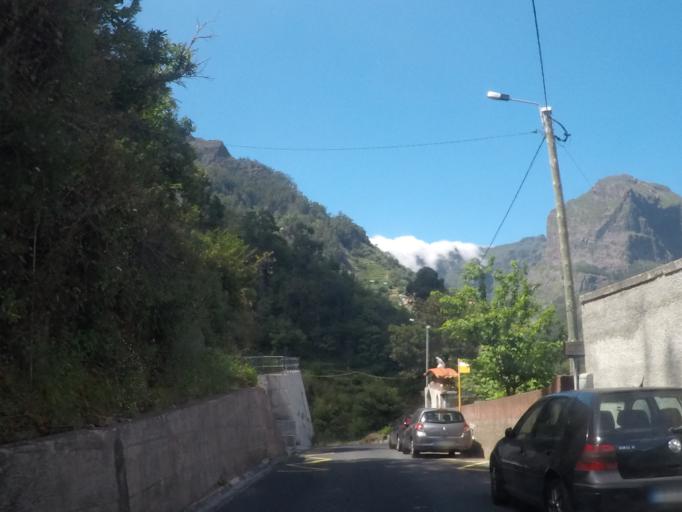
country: PT
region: Madeira
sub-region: Camara de Lobos
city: Curral das Freiras
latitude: 32.7101
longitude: -16.9732
